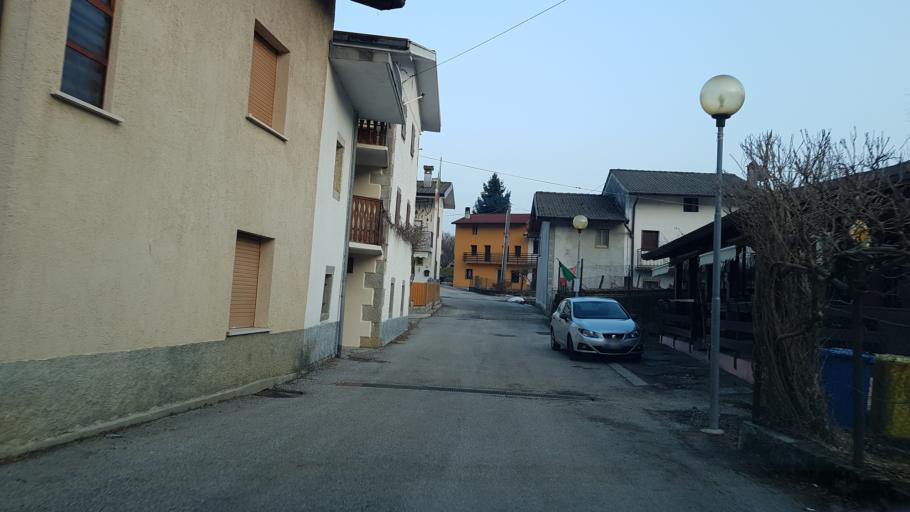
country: IT
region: Friuli Venezia Giulia
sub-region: Provincia di Udine
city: Taipana
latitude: 46.2413
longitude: 13.3847
